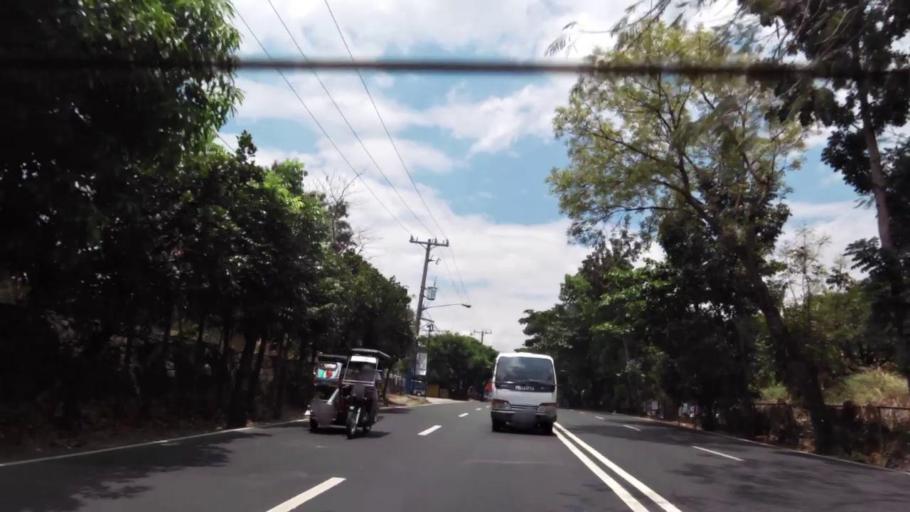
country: PH
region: Calabarzon
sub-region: Province of Rizal
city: Antipolo
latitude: 14.6115
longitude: 121.1580
